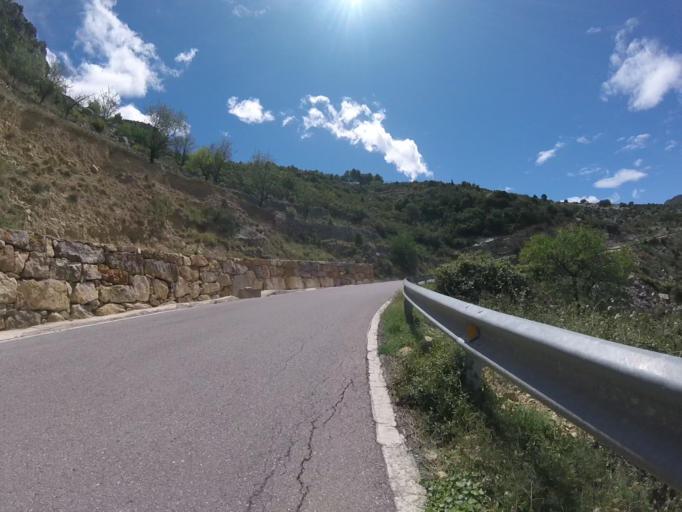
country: ES
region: Valencia
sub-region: Provincia de Castello
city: Sierra-Engarceran
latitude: 40.2826
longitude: -0.0316
